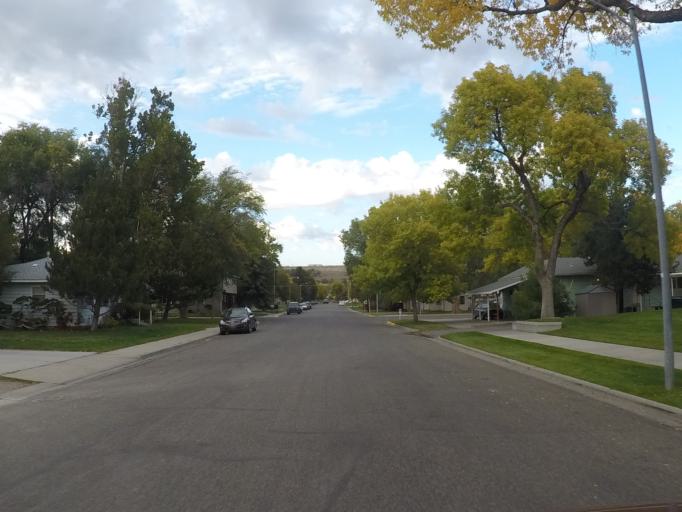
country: US
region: Montana
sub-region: Yellowstone County
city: Billings
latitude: 45.7874
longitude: -108.5306
